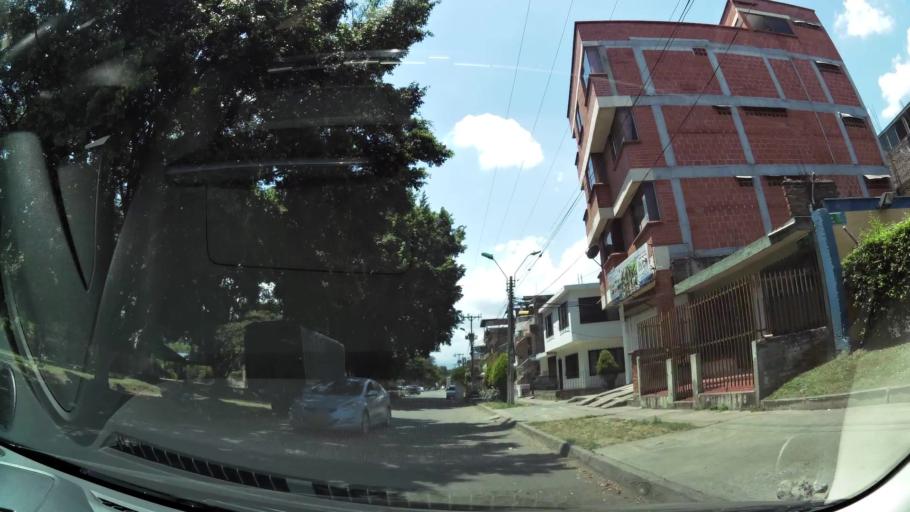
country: CO
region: Valle del Cauca
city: Cali
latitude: 3.4483
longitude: -76.4891
